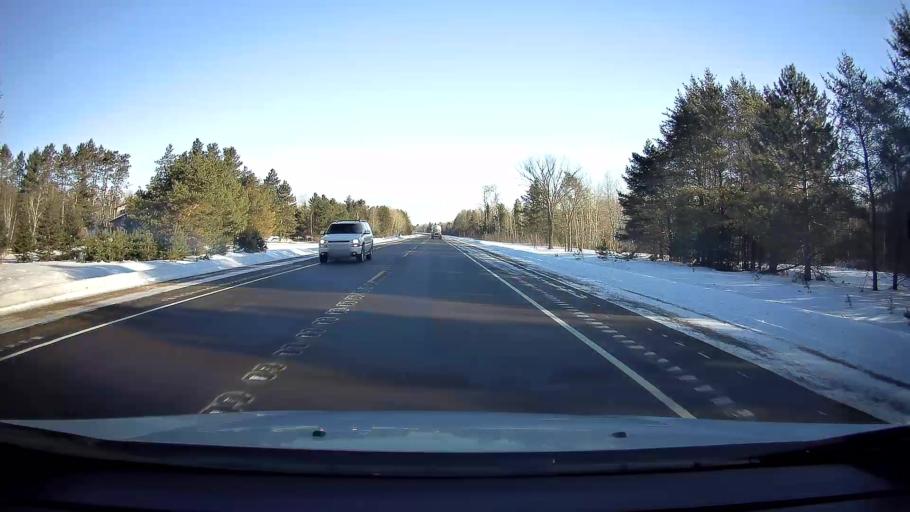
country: US
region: Wisconsin
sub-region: Sawyer County
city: Hayward
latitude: 46.0891
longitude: -91.3919
